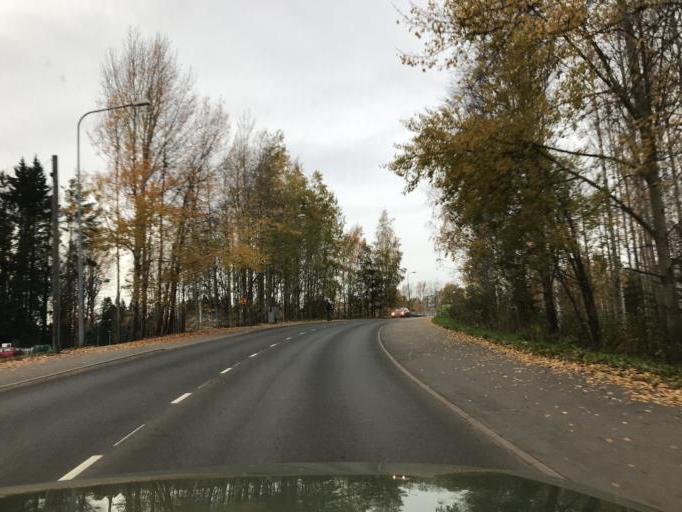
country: FI
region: Uusimaa
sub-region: Helsinki
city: Vantaa
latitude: 60.2520
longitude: 25.0814
